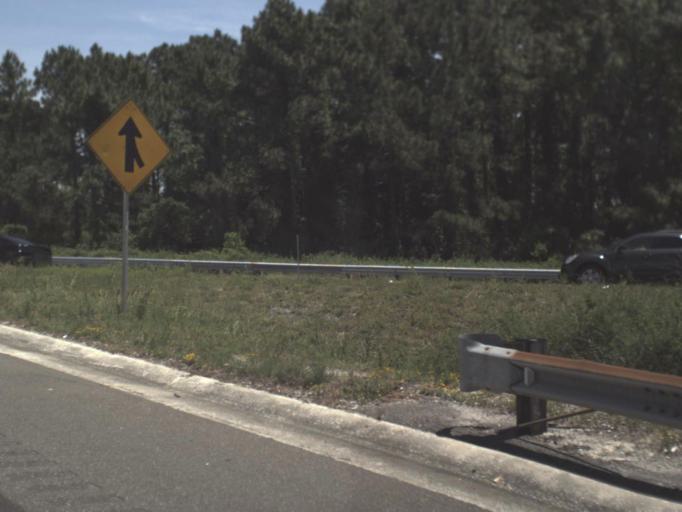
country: US
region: Florida
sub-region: Clay County
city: Orange Park
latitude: 30.1914
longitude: -81.7067
